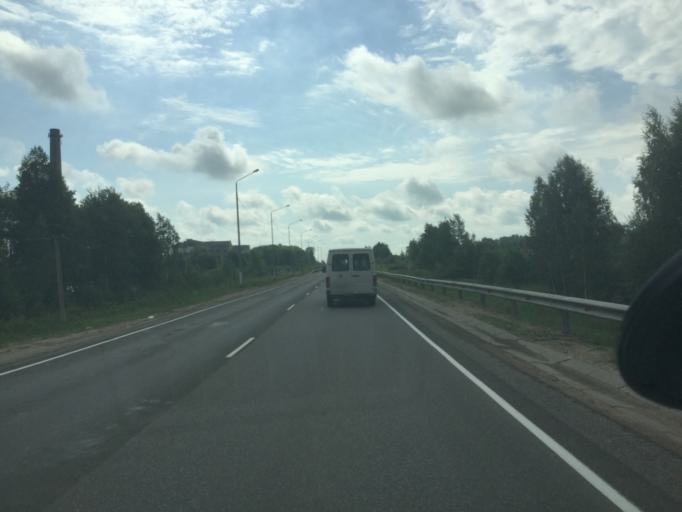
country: RU
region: Smolensk
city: Golynki
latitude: 54.8661
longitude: 31.3574
